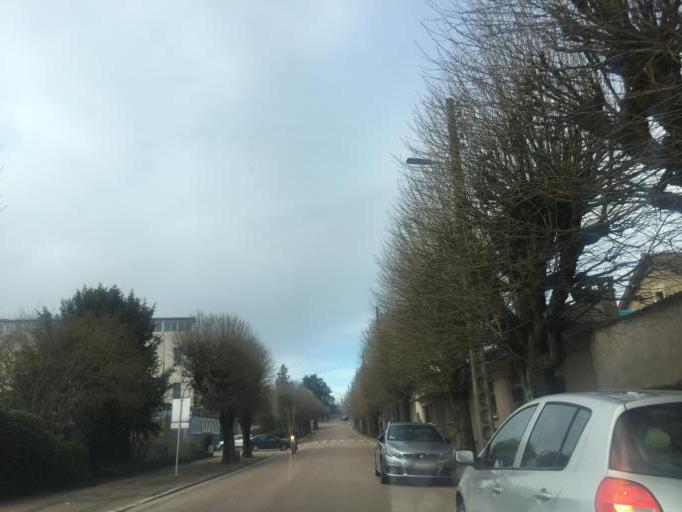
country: FR
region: Bourgogne
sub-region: Departement de la Nievre
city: Clamecy
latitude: 47.4630
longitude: 3.5199
